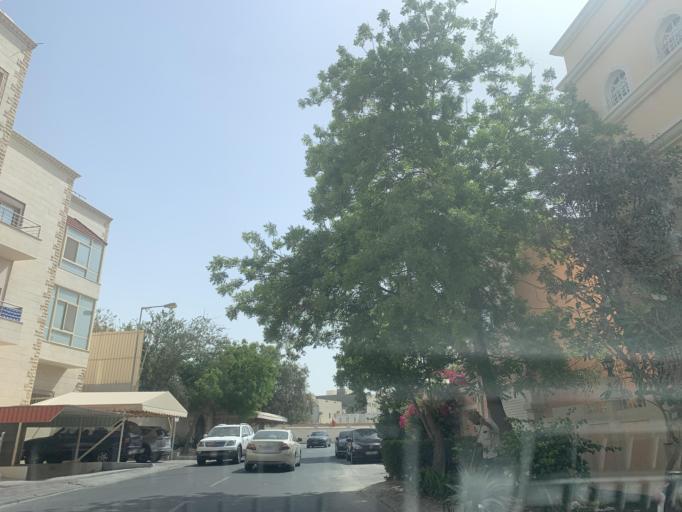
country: BH
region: Northern
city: Ar Rifa'
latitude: 26.1449
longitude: 50.5667
